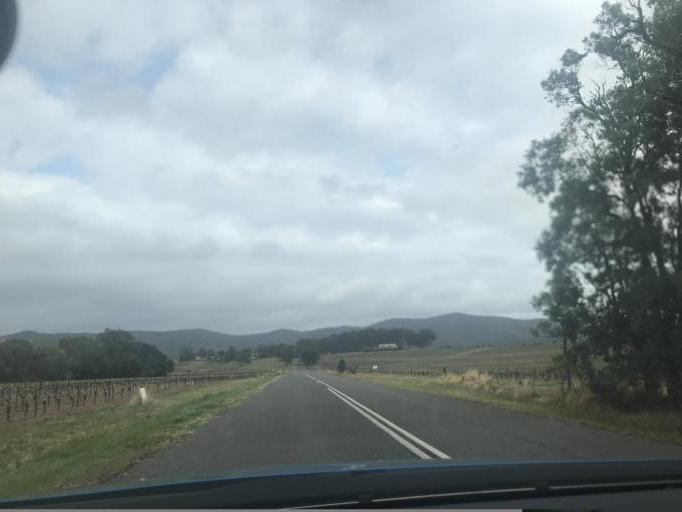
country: AU
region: New South Wales
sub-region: Cessnock
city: Cessnock
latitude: -32.8095
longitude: 151.2940
